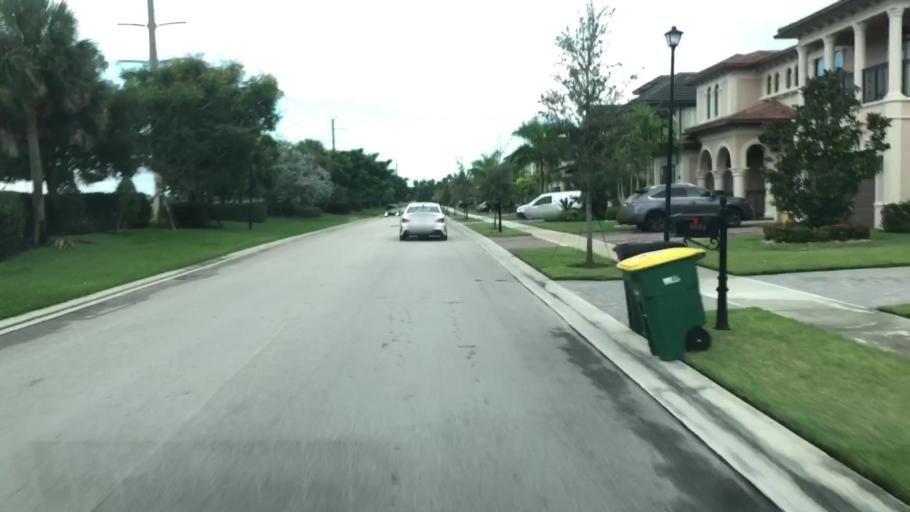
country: US
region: Florida
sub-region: Broward County
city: Parkland
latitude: 26.3394
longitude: -80.2755
